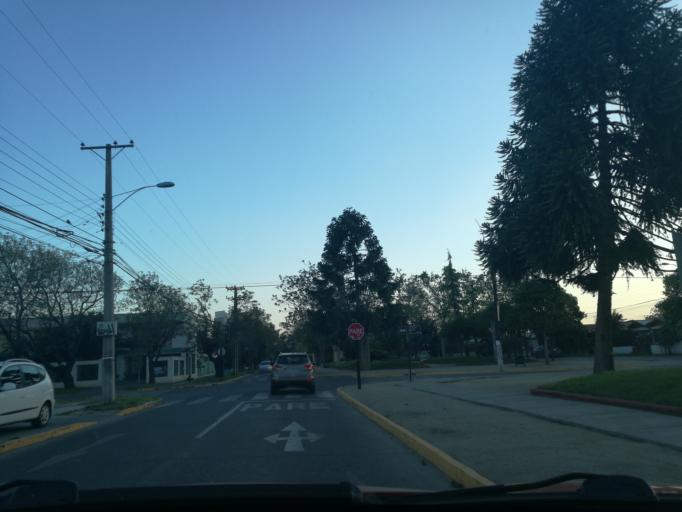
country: CL
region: O'Higgins
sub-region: Provincia de Cachapoal
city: Rancagua
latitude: -34.1604
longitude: -70.7360
